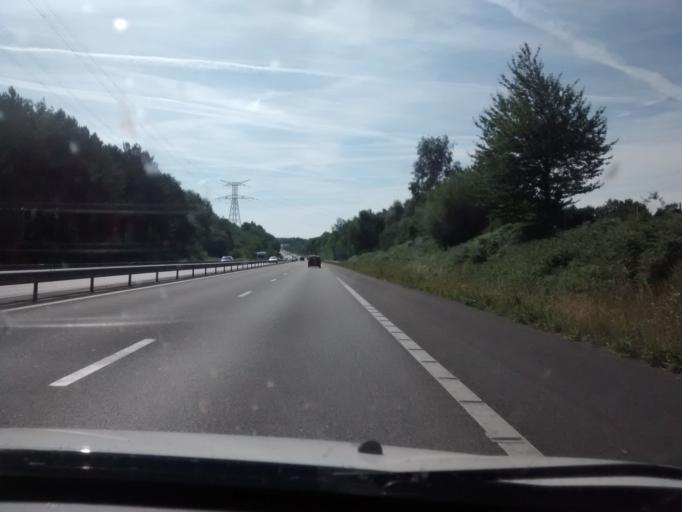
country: FR
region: Pays de la Loire
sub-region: Departement de la Mayenne
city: Saint-Pierre-la-Cour
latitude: 48.0868
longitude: -1.0624
